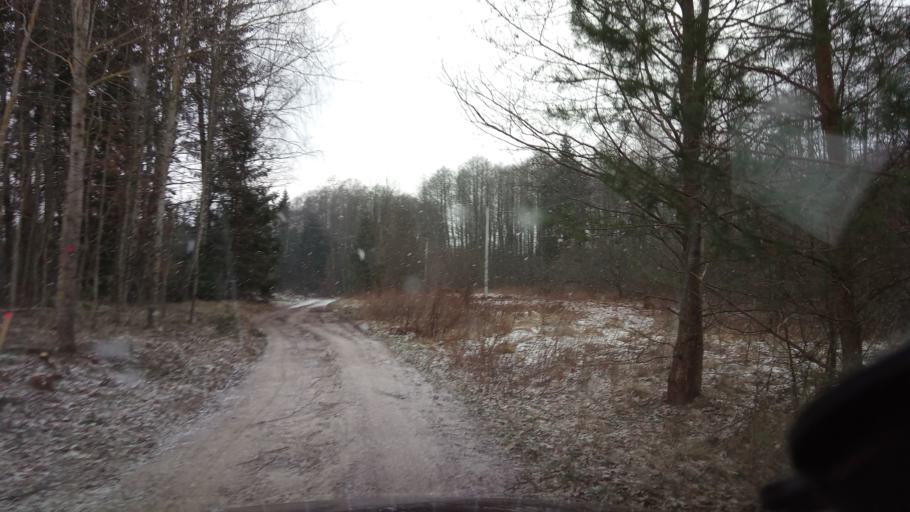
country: LT
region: Alytaus apskritis
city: Varena
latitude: 54.1273
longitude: 24.6774
